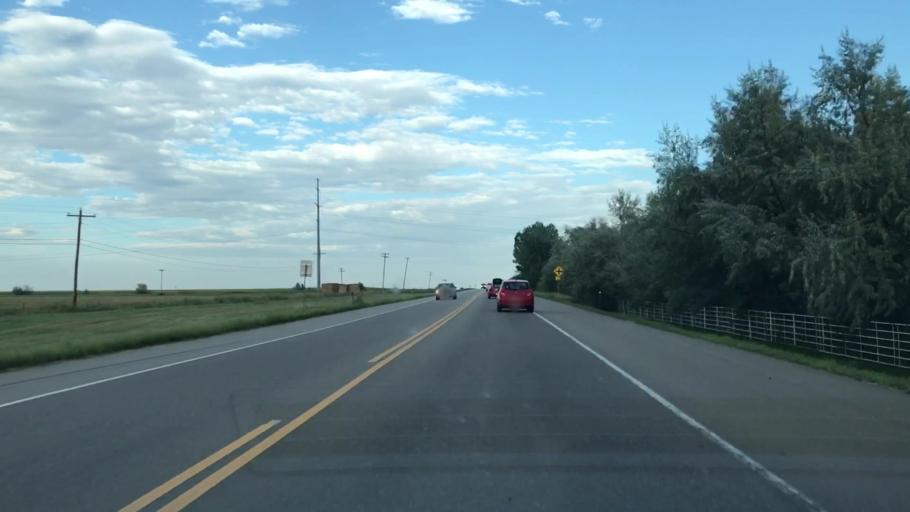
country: US
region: Colorado
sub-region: Weld County
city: Mead
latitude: 40.2038
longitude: -105.0396
